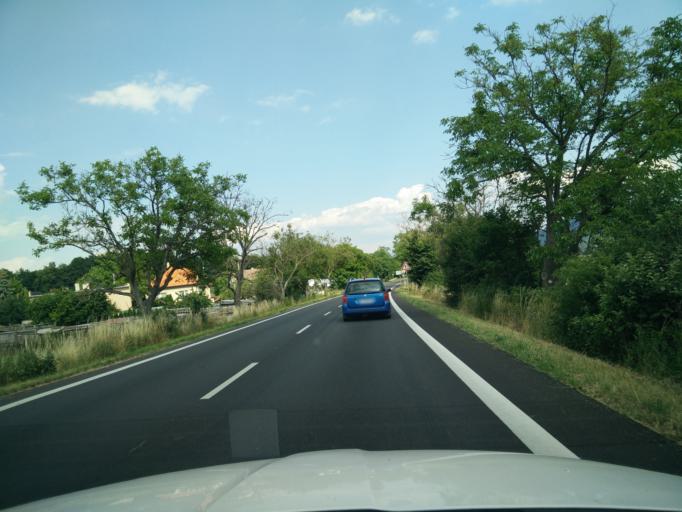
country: SK
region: Nitriansky
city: Partizanske
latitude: 48.6308
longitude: 18.3293
